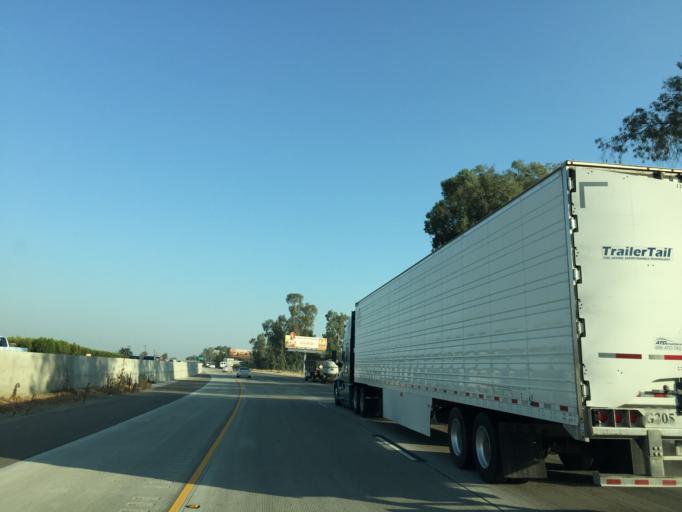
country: US
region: California
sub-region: Fresno County
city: Kingsburg
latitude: 36.4851
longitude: -119.5105
